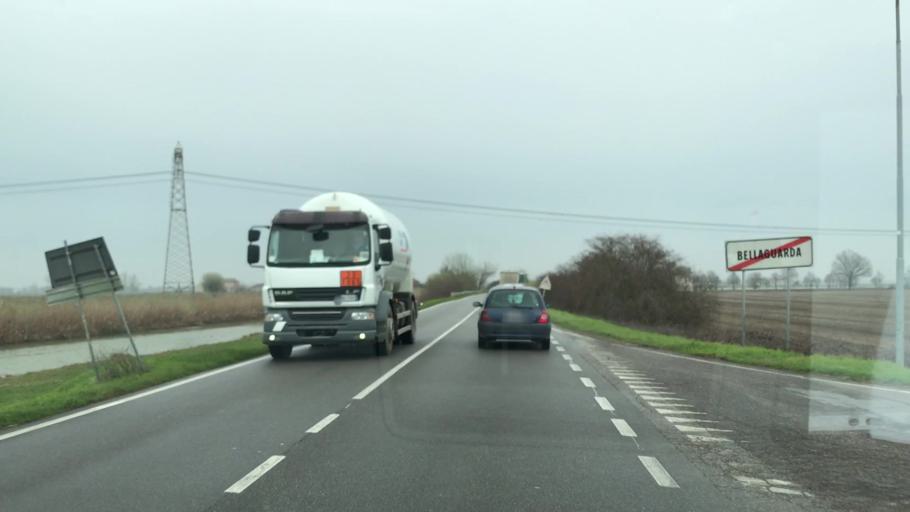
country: IT
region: Lombardy
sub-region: Provincia di Mantova
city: Commessaggio
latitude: 45.0001
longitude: 10.5860
